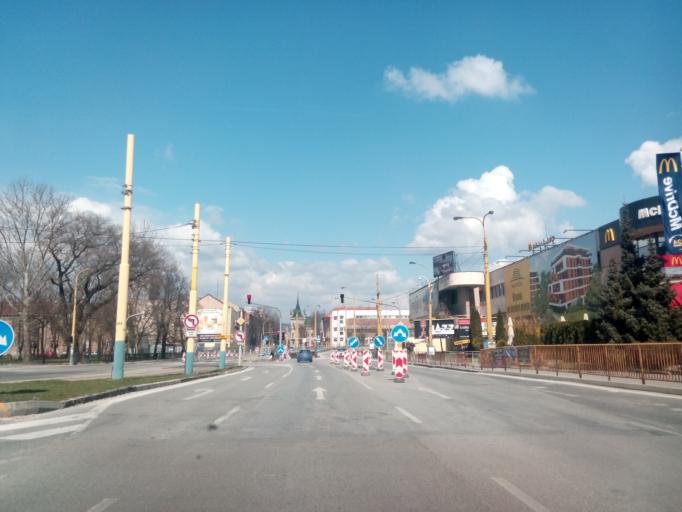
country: SK
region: Kosicky
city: Kosice
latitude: 48.7190
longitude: 21.2650
